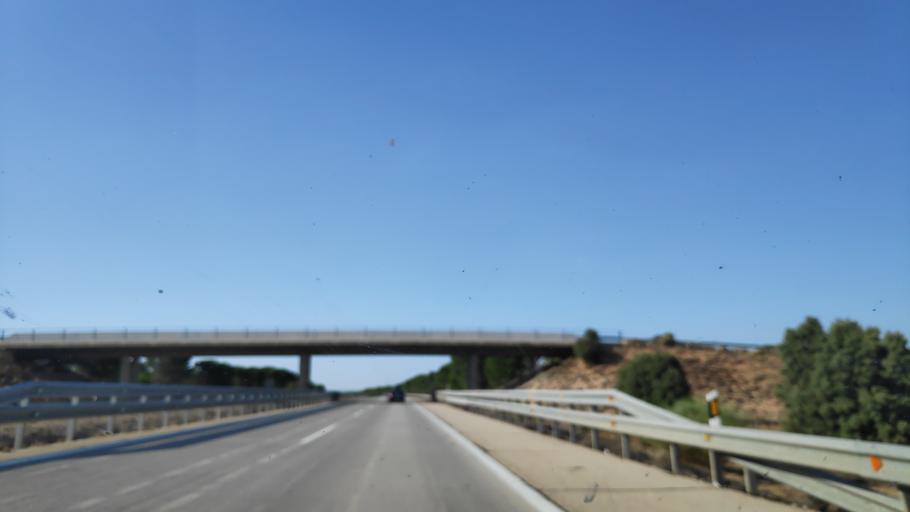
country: ES
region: Castille-La Mancha
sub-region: Provincia de Cuenca
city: Pozoamargo
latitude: 39.3305
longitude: -2.2007
